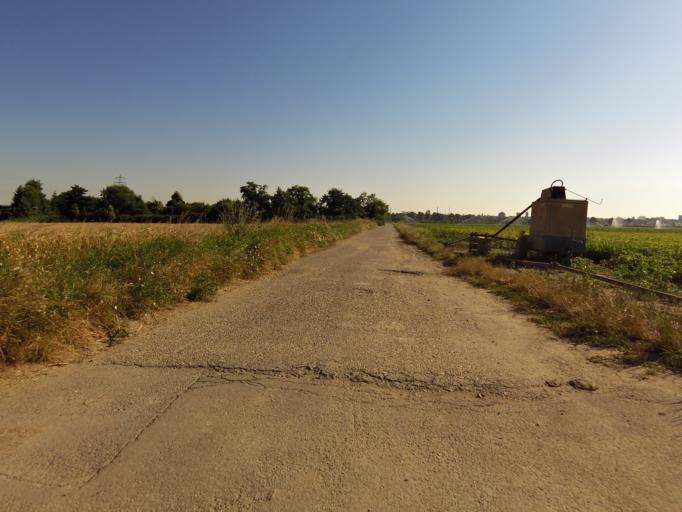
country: DE
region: Rheinland-Pfalz
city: Gartenstadt
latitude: 49.4808
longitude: 8.3974
